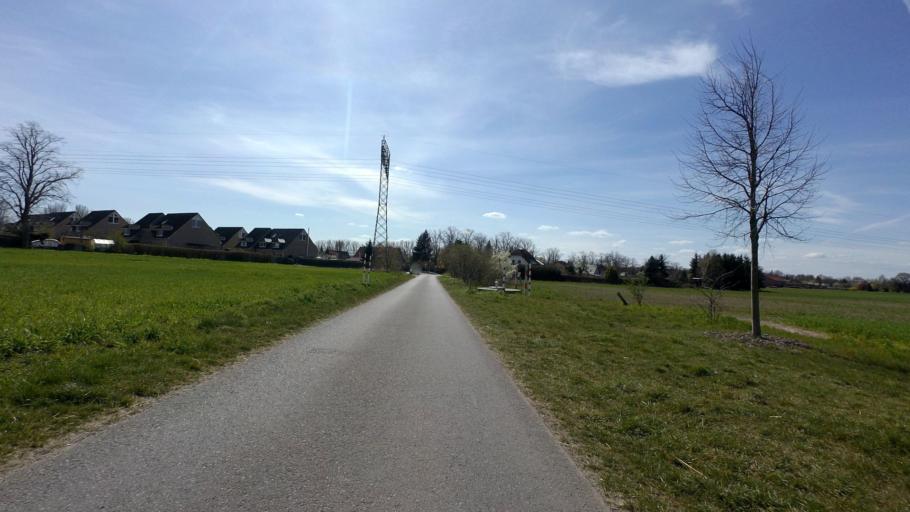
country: DE
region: Brandenburg
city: Schonefeld
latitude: 52.3450
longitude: 13.5200
